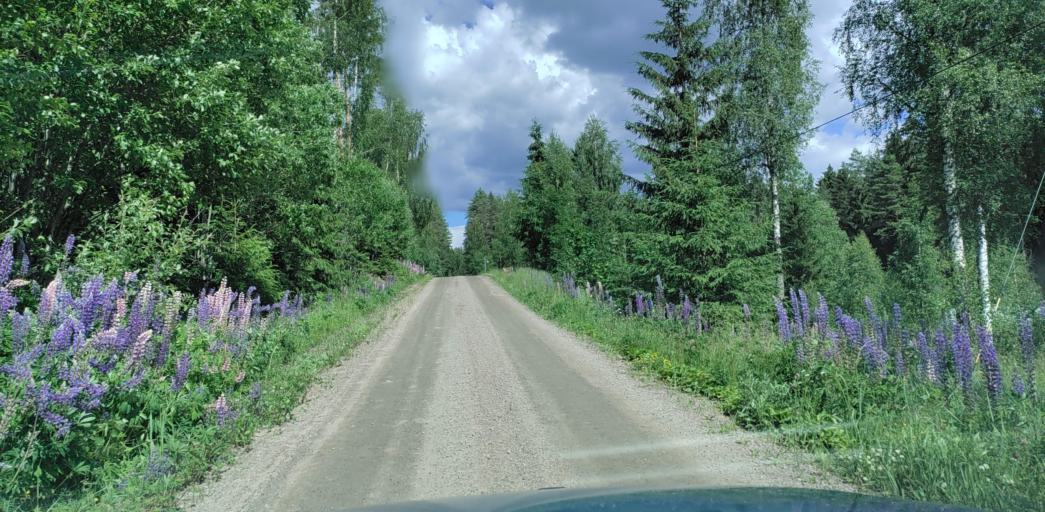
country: SE
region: Vaermland
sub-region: Sunne Kommun
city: Sunne
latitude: 60.0391
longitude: 13.2472
